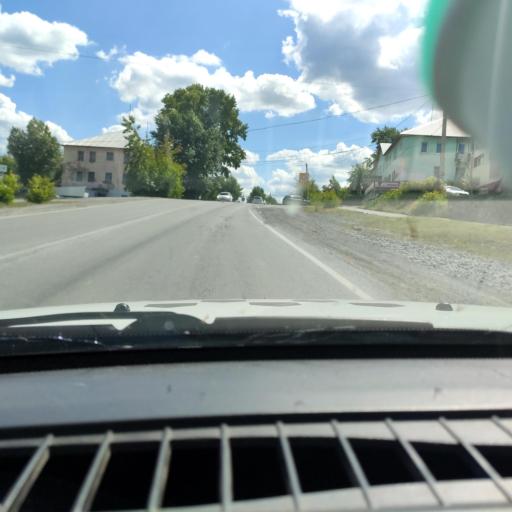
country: RU
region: Chelyabinsk
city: Satka
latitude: 55.0462
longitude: 58.9824
